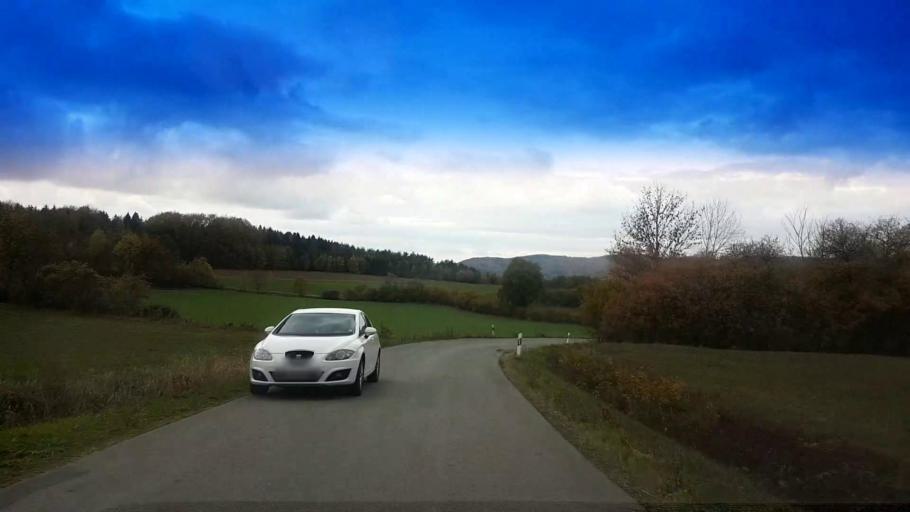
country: DE
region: Bavaria
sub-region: Upper Franconia
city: Wattendorf
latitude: 50.0200
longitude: 11.1078
